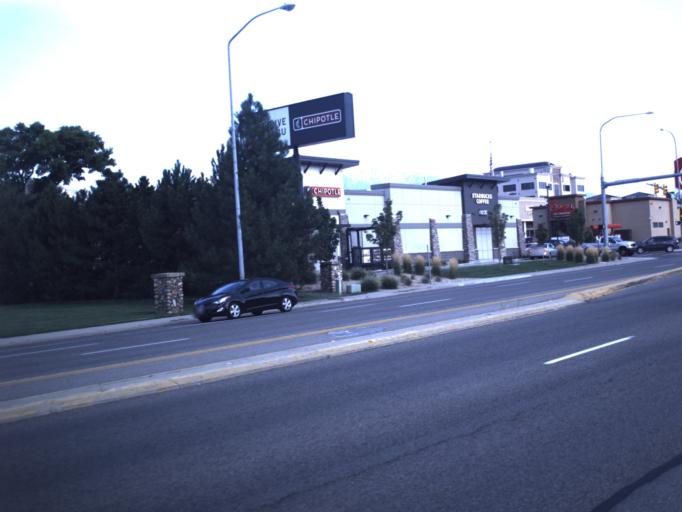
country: US
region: Utah
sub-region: Salt Lake County
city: Murray
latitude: 40.6602
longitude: -111.8884
